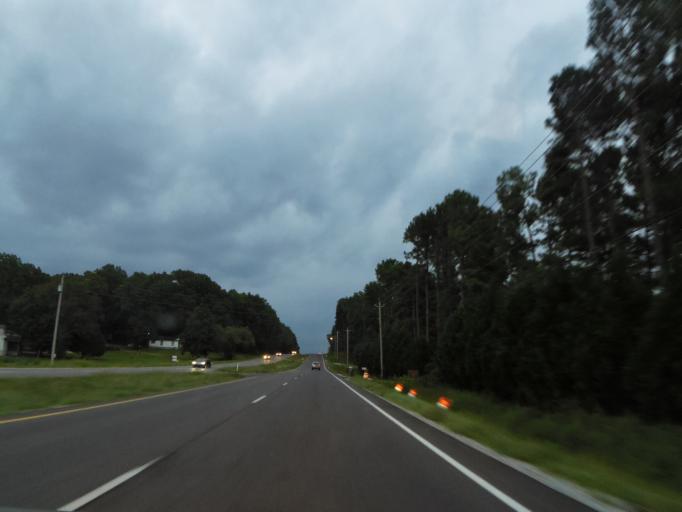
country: US
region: Alabama
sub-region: Madison County
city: Moores Mill
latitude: 34.7643
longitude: -86.4853
